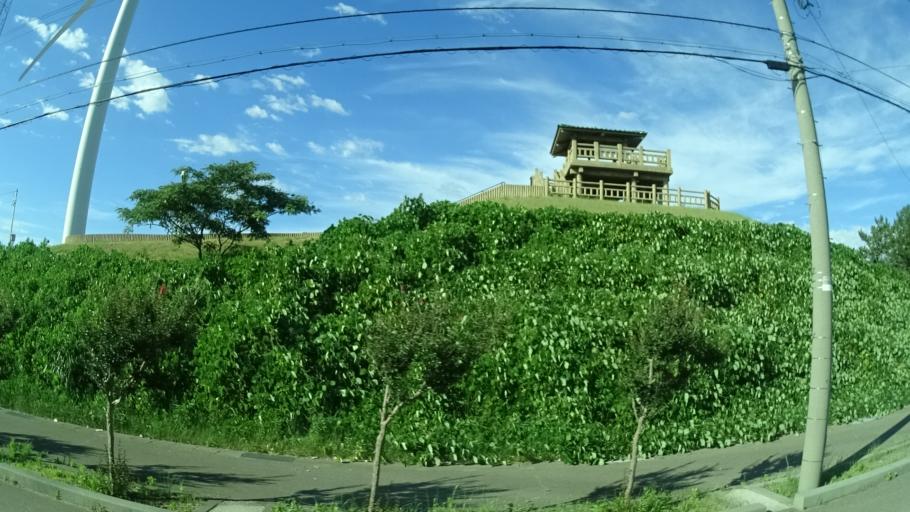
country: JP
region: Ishikawa
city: Kanazawa-shi
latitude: 36.6630
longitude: 136.6502
